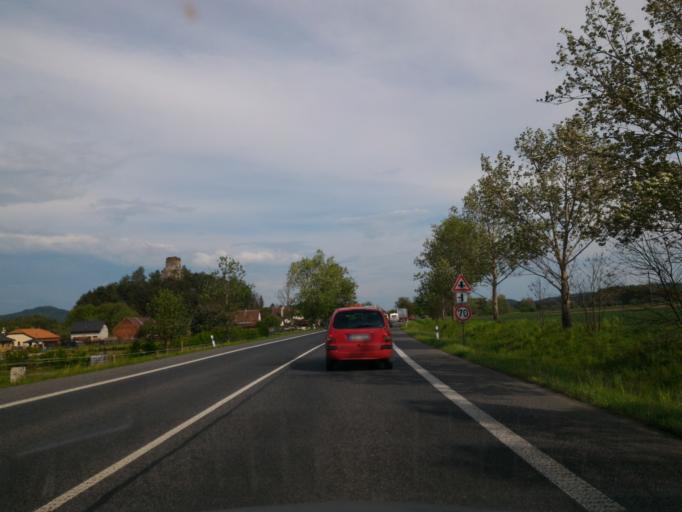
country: CZ
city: Duba
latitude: 50.6132
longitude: 14.5735
